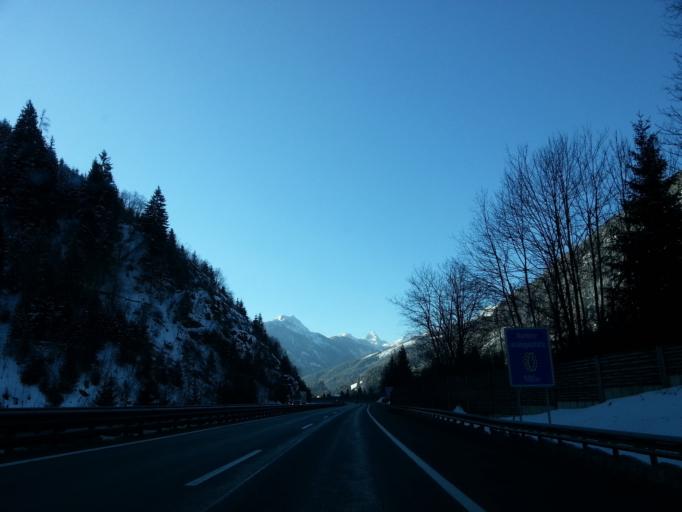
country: AT
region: Salzburg
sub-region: Politischer Bezirk Sankt Johann im Pongau
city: Flachau
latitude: 47.3247
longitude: 13.3947
